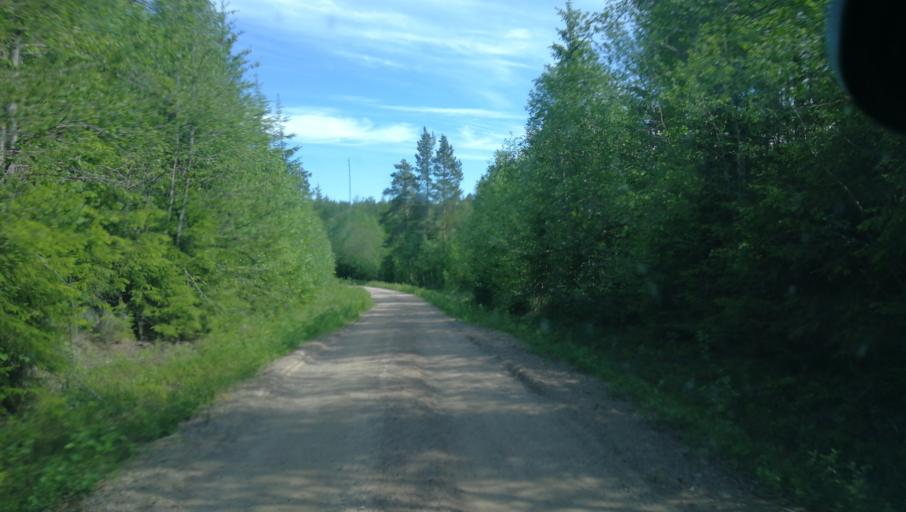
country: SE
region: Dalarna
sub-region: Vansbro Kommun
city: Vansbro
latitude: 60.8250
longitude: 14.1667
